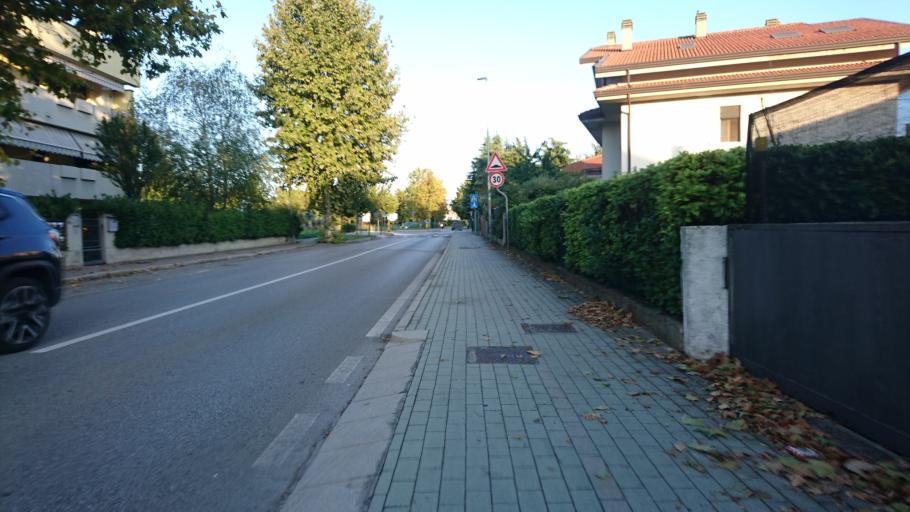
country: IT
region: Veneto
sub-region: Provincia di Padova
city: Montegrotto Terme
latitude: 45.3397
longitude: 11.7865
